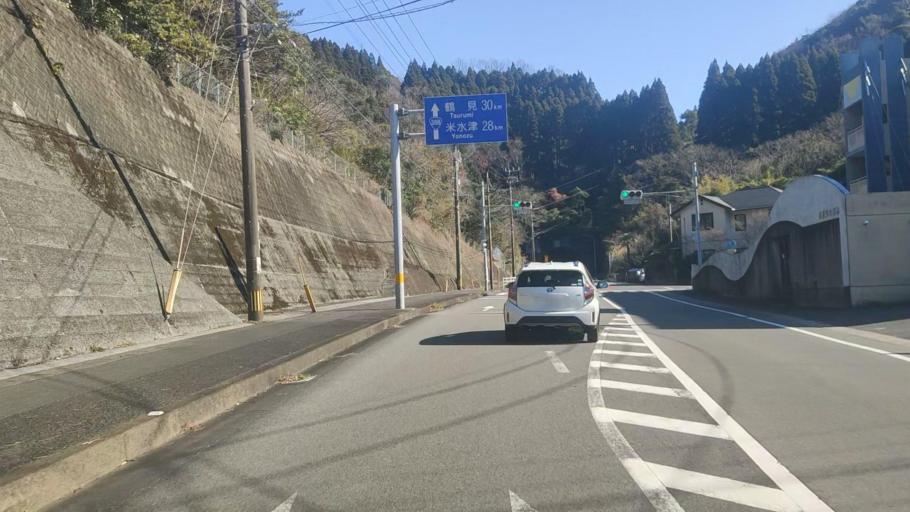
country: JP
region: Oita
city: Saiki
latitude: 32.8007
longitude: 131.9308
